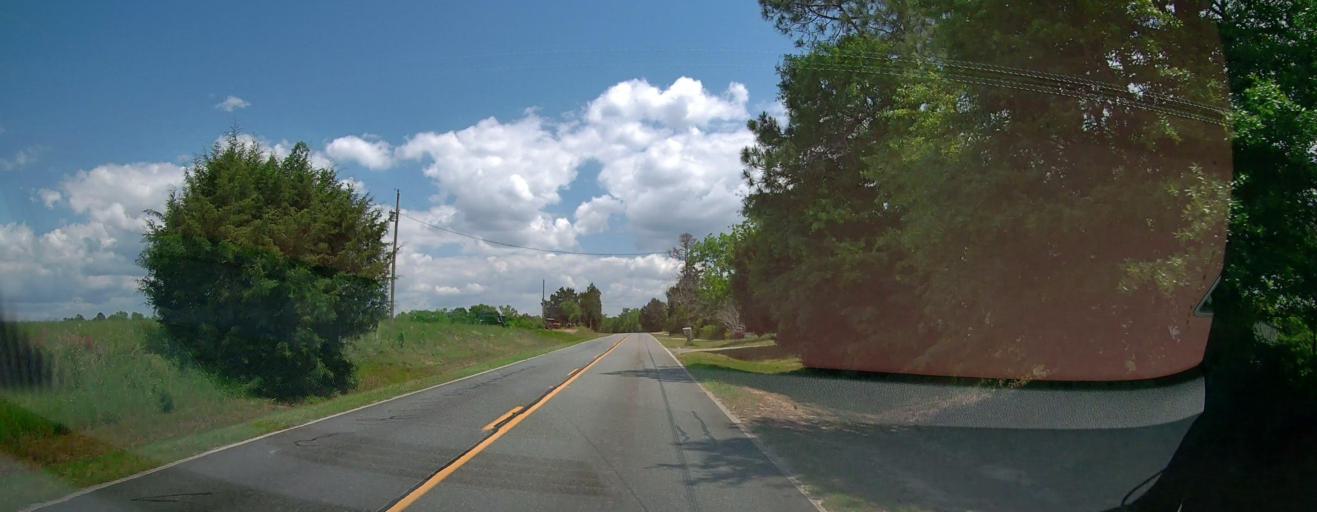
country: US
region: Georgia
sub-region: Treutlen County
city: Soperton
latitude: 32.5126
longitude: -82.6478
